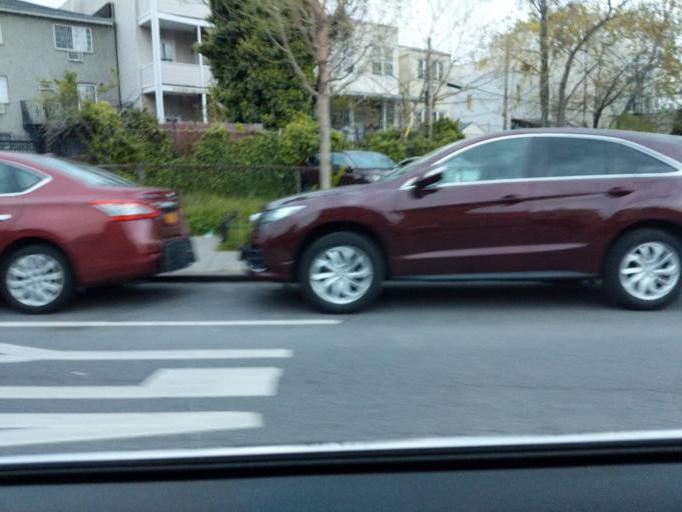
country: US
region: New York
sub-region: Bronx
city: The Bronx
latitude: 40.8404
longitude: -73.8529
